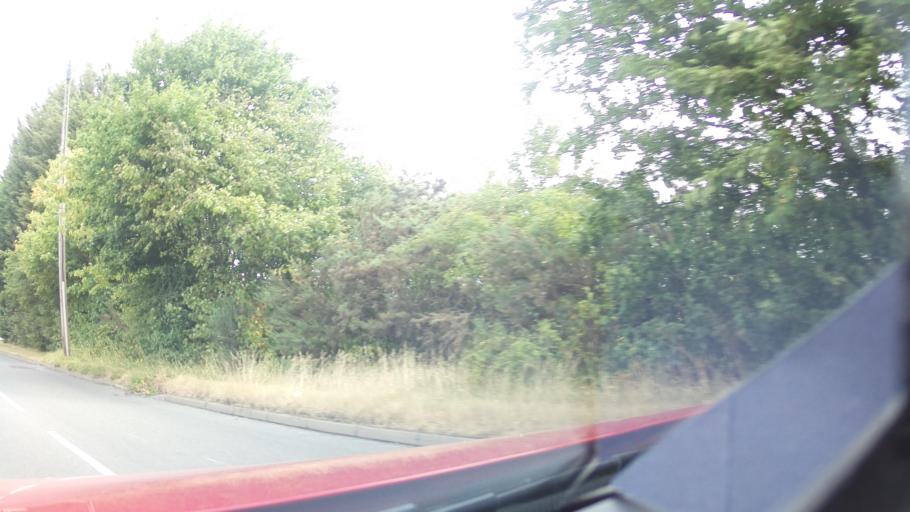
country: GB
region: England
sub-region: Derbyshire
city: Ilkeston
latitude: 52.9422
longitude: -1.3092
